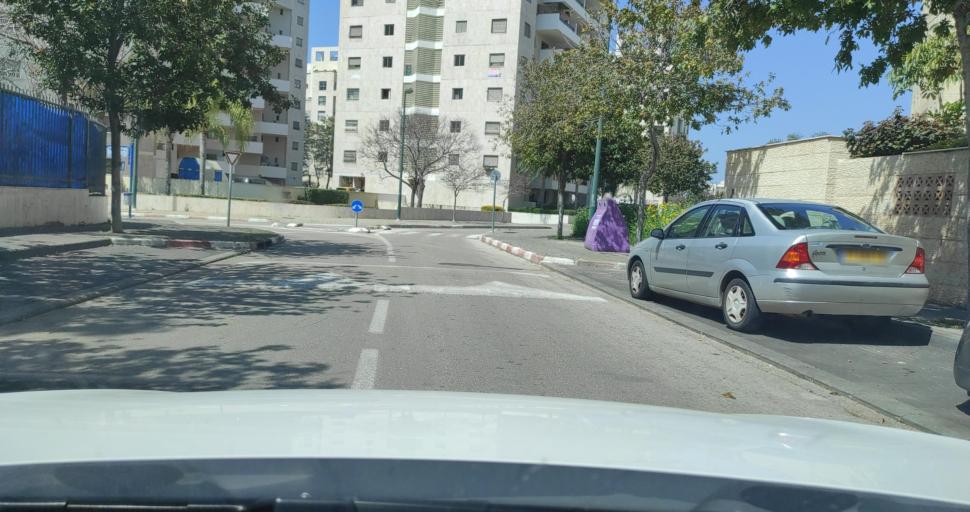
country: IL
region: Central District
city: Nordiyya
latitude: 32.3021
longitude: 34.8719
